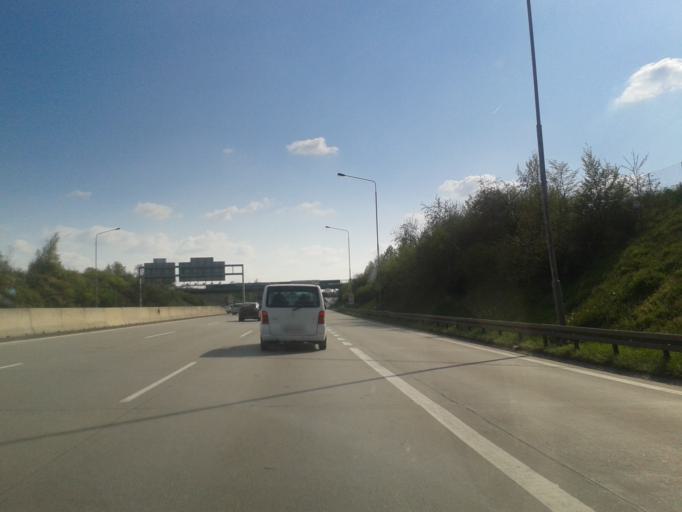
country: CZ
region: Central Bohemia
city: Hostivice
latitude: 50.0725
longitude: 14.2872
